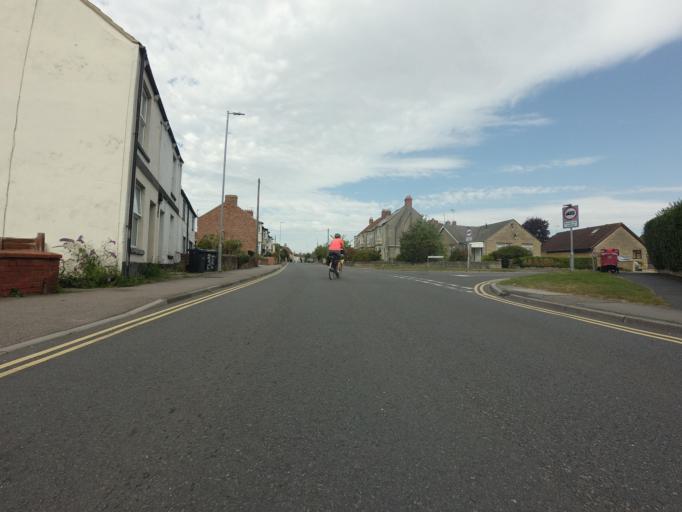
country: GB
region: England
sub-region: Wiltshire
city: Trowbridge
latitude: 51.3259
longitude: -2.2041
